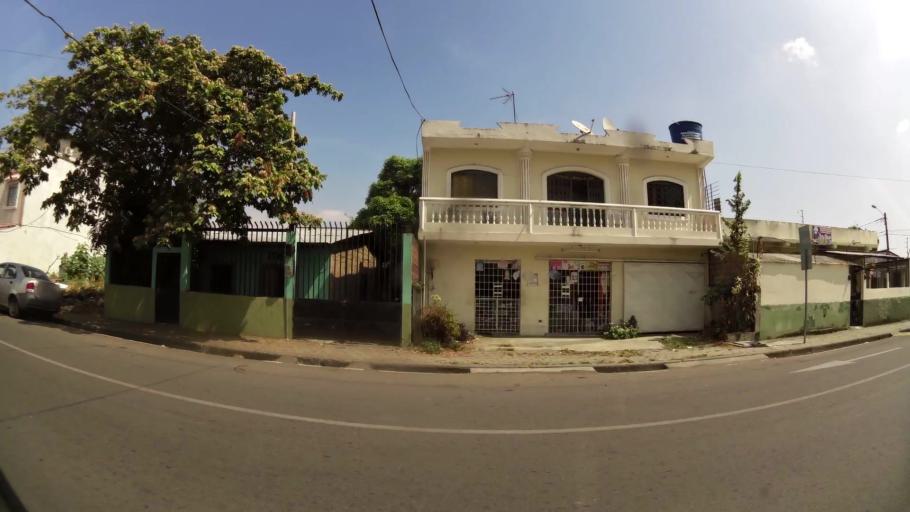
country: EC
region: Guayas
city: Eloy Alfaro
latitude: -2.1566
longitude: -79.8410
